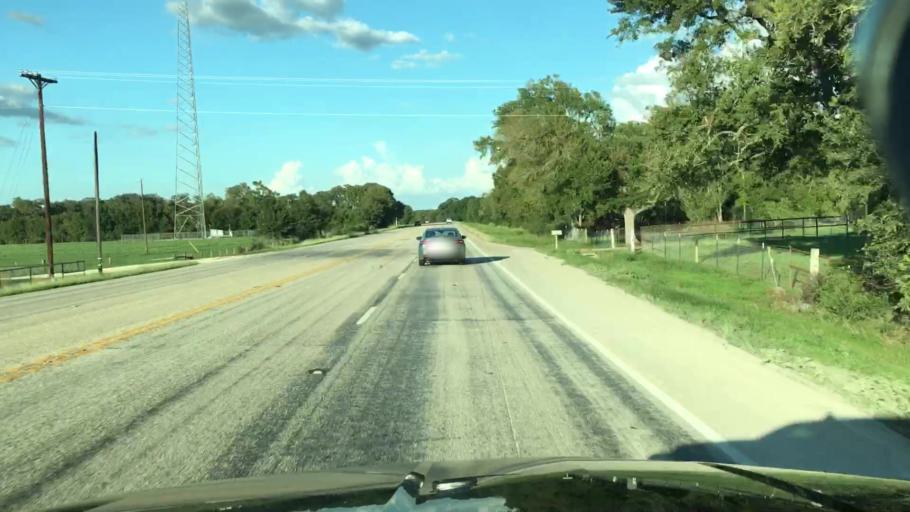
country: US
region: Texas
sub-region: Lee County
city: Lexington
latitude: 30.3307
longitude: -96.9136
